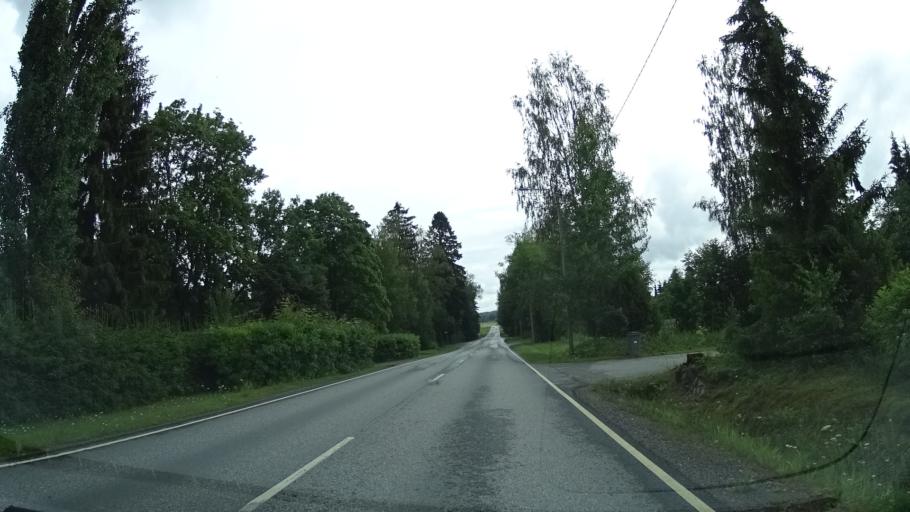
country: FI
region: Haeme
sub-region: Forssa
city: Humppila
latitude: 61.1014
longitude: 23.2875
